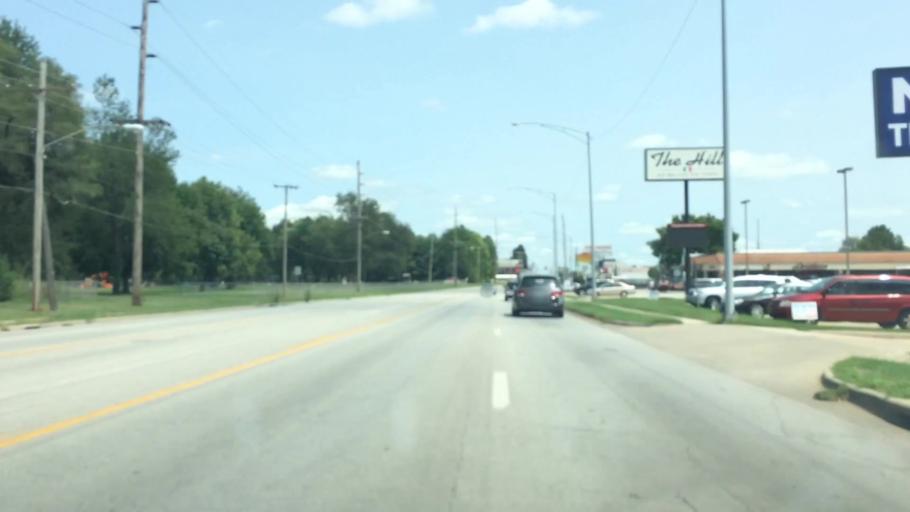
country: US
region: Missouri
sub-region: Greene County
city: Springfield
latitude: 37.1599
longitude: -93.2895
